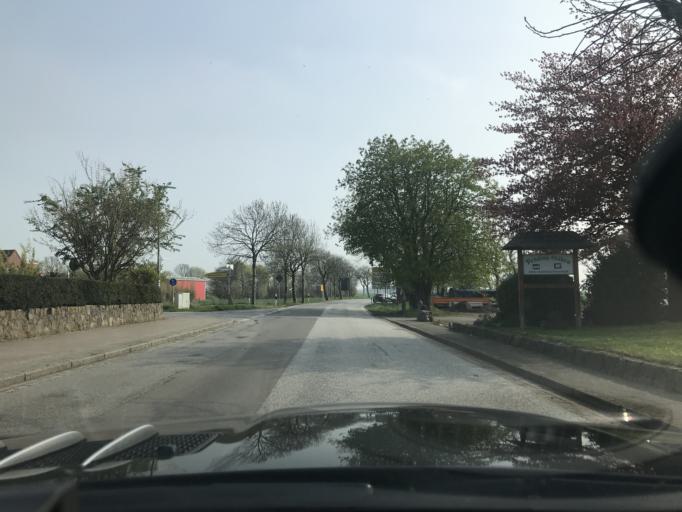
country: DE
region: Schleswig-Holstein
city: Fehmarn
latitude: 54.4930
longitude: 11.2102
